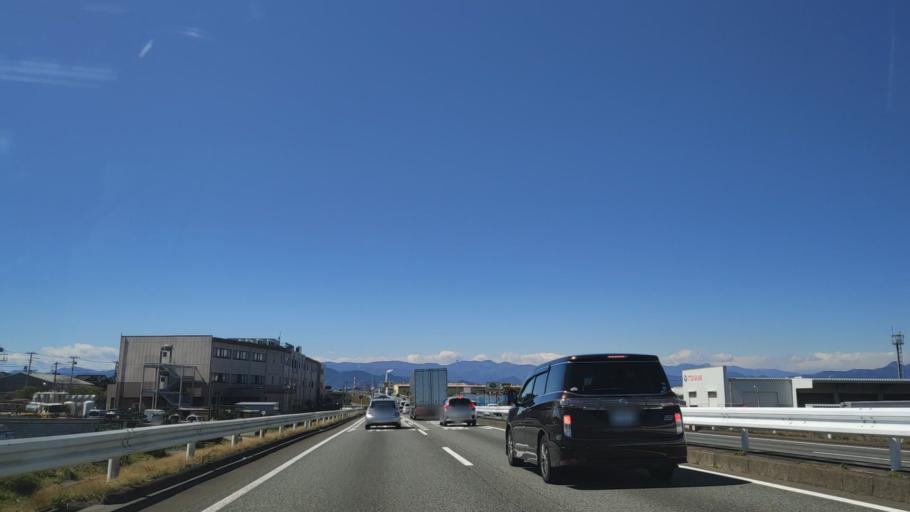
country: JP
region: Shizuoka
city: Fuji
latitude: 35.1378
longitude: 138.7505
